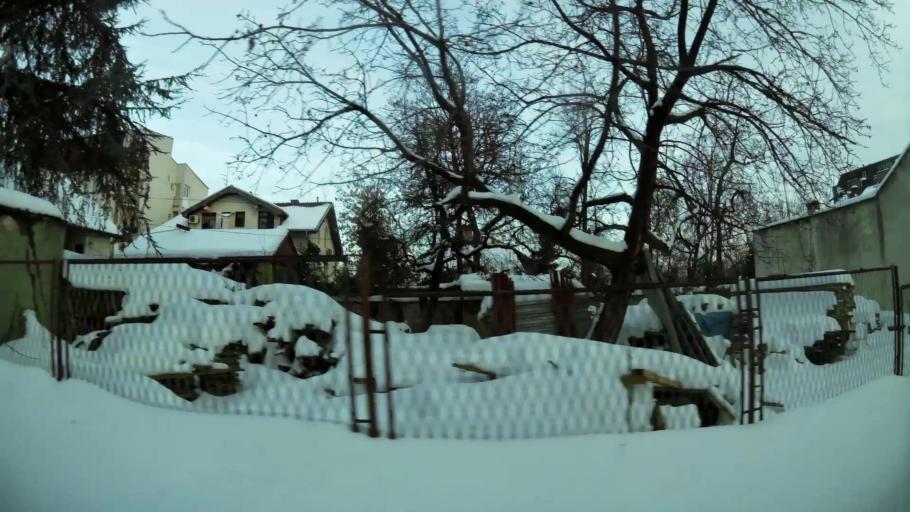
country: RS
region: Central Serbia
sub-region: Belgrade
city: Palilula
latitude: 44.7932
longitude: 20.5167
